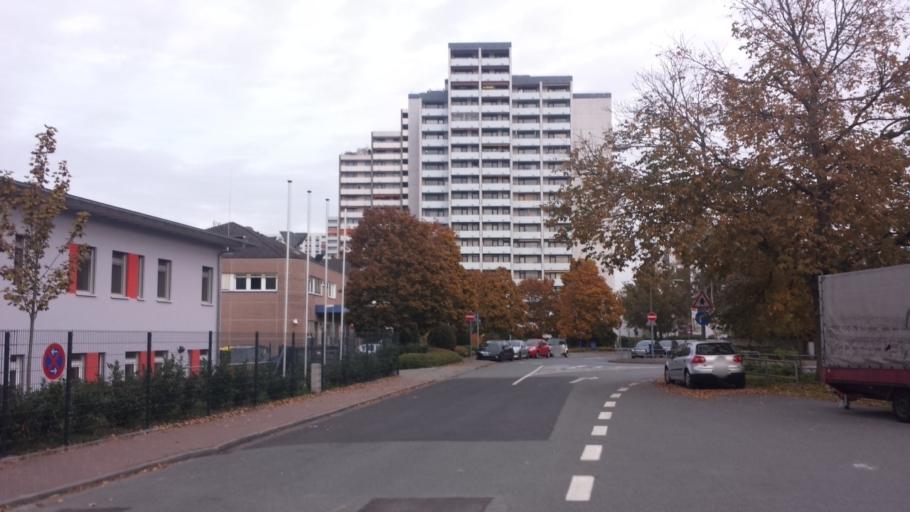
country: DE
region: Hesse
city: Niederrad
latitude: 50.0878
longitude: 8.6347
